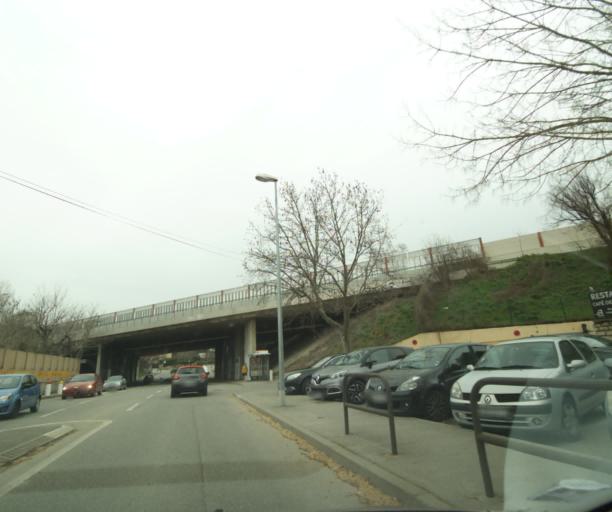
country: FR
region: Provence-Alpes-Cote d'Azur
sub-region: Departement des Bouches-du-Rhone
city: Meyreuil
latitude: 43.5106
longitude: 5.4757
